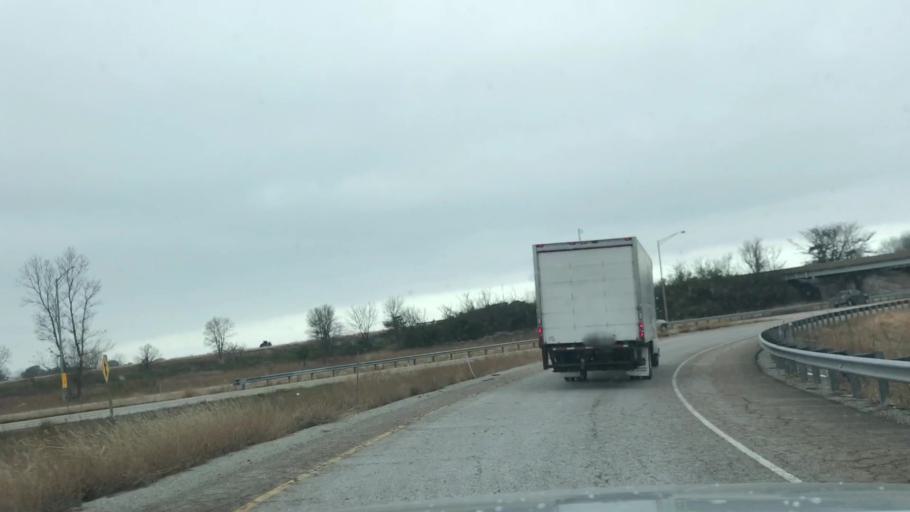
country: US
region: Illinois
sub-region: Madison County
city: Troy
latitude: 38.7507
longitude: -89.9069
